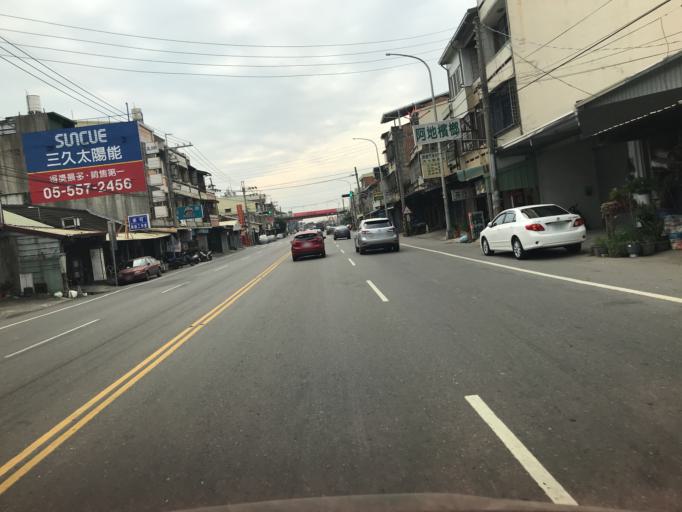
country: TW
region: Taiwan
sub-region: Yunlin
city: Douliu
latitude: 23.7429
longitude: 120.6051
